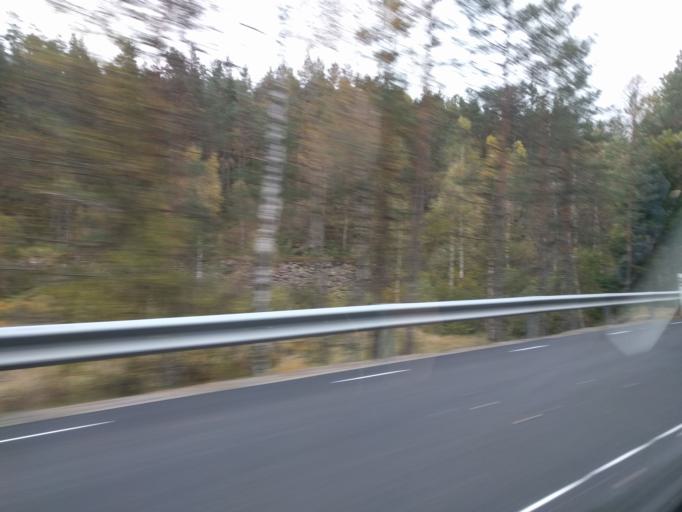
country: NO
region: Aust-Agder
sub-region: Iveland
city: Birketveit
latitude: 58.4442
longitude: 7.7913
